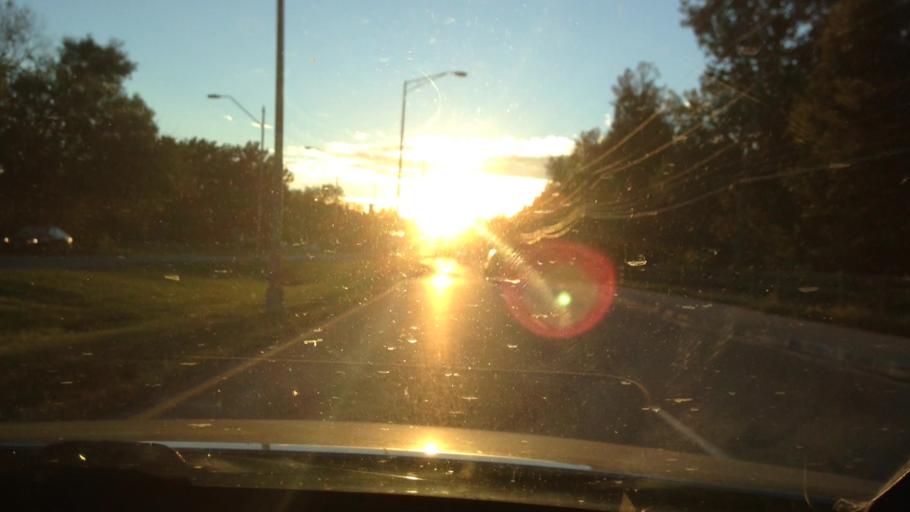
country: US
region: Missouri
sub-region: Jackson County
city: Raytown
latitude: 39.0151
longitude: -94.5191
